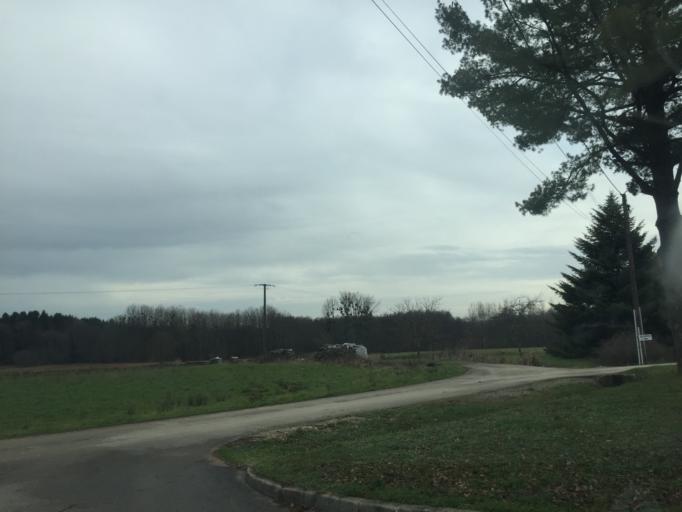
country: FR
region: Franche-Comte
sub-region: Departement du Jura
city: Mont-sous-Vaudrey
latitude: 46.8677
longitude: 5.5328
